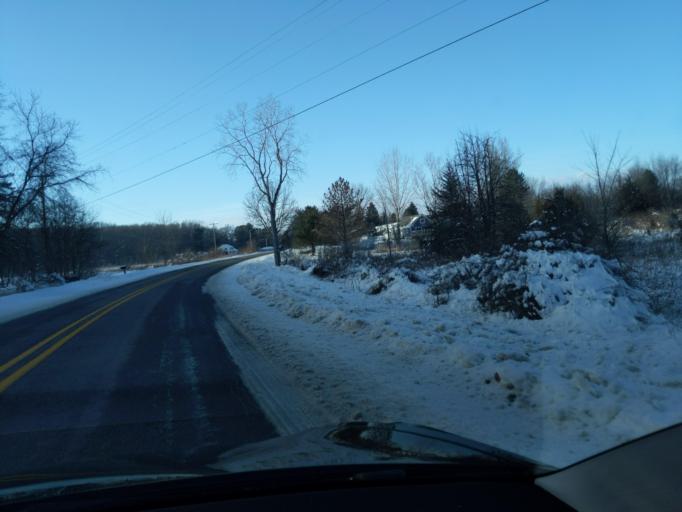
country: US
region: Michigan
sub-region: Ingham County
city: Stockbridge
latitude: 42.4322
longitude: -84.0885
